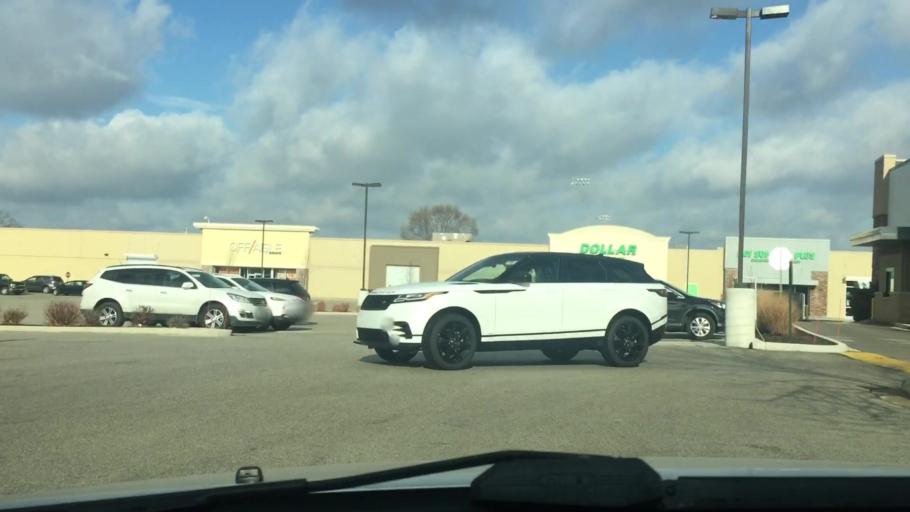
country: US
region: Wisconsin
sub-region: Waukesha County
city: Waukesha
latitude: 42.9885
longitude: -88.2240
